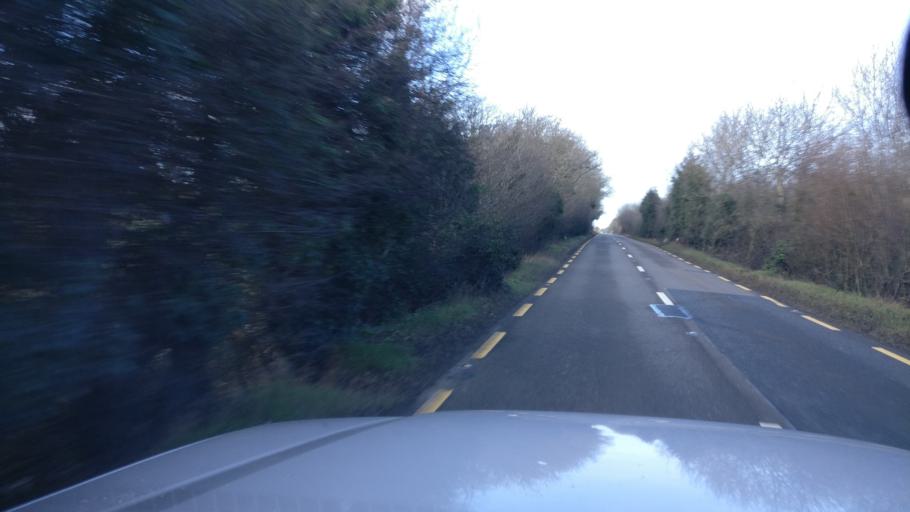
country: IE
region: Leinster
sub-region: Laois
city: Mountmellick
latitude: 53.0799
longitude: -7.3311
